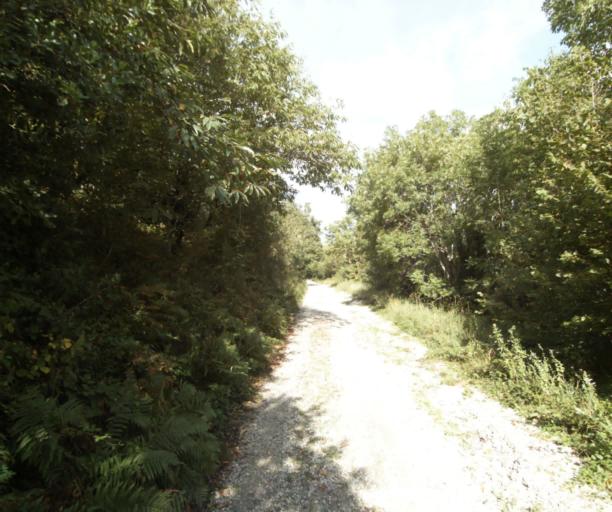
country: FR
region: Midi-Pyrenees
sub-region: Departement du Tarn
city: Dourgne
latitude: 43.4606
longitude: 2.1146
